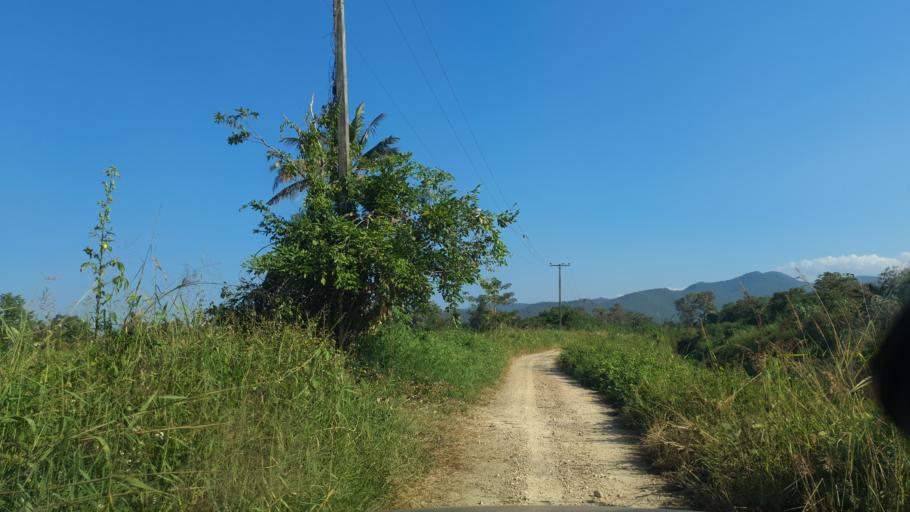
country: TH
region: Chiang Mai
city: San Kamphaeng
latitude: 18.7285
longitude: 99.1792
